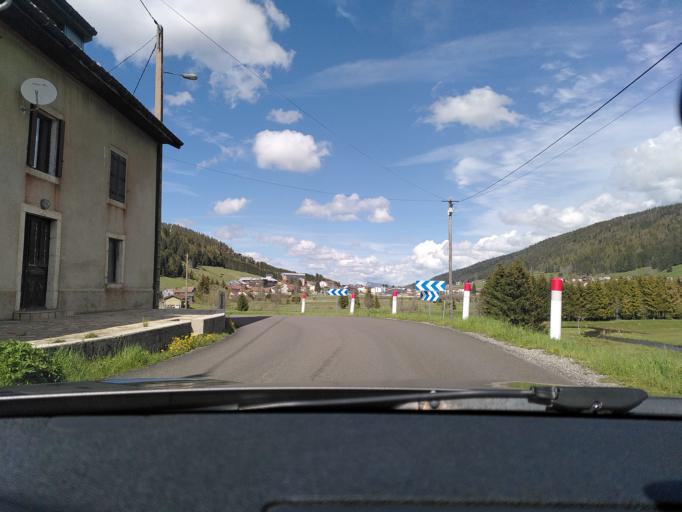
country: FR
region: Franche-Comte
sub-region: Departement du Jura
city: Les Rousses
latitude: 46.5332
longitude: 6.1297
